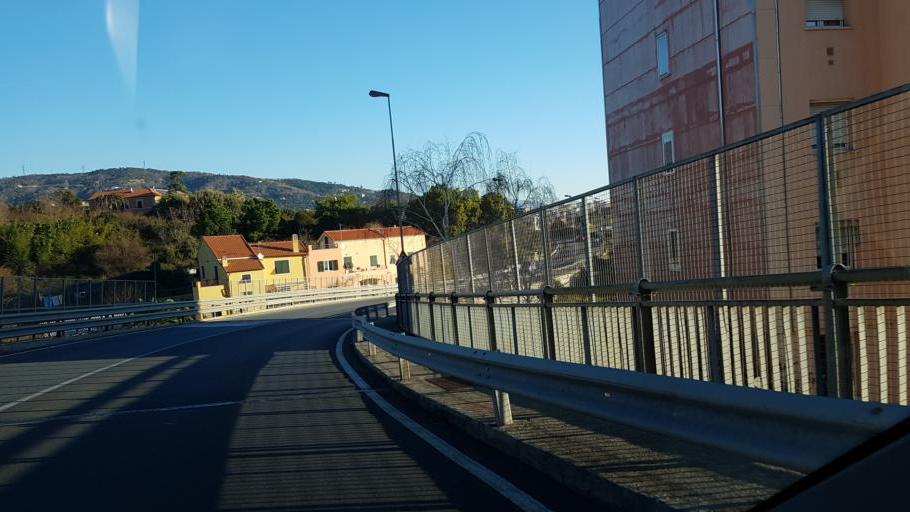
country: IT
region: Liguria
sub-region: Provincia di Savona
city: Valleggia
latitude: 44.2954
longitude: 8.4472
